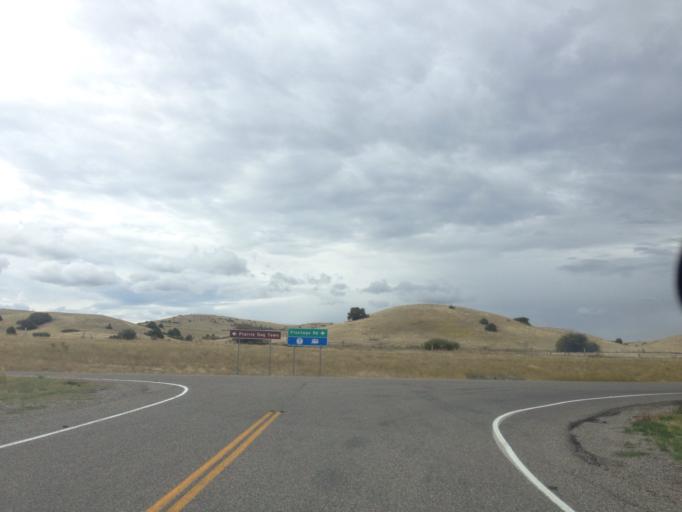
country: US
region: Montana
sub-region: Sweet Grass County
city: Big Timber
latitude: 45.7687
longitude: -109.7949
